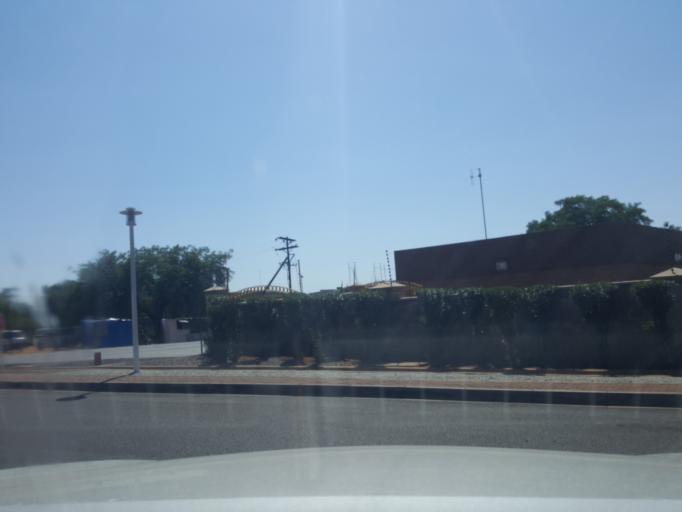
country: BW
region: South East
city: Gaborone
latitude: -24.6951
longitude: 25.8787
